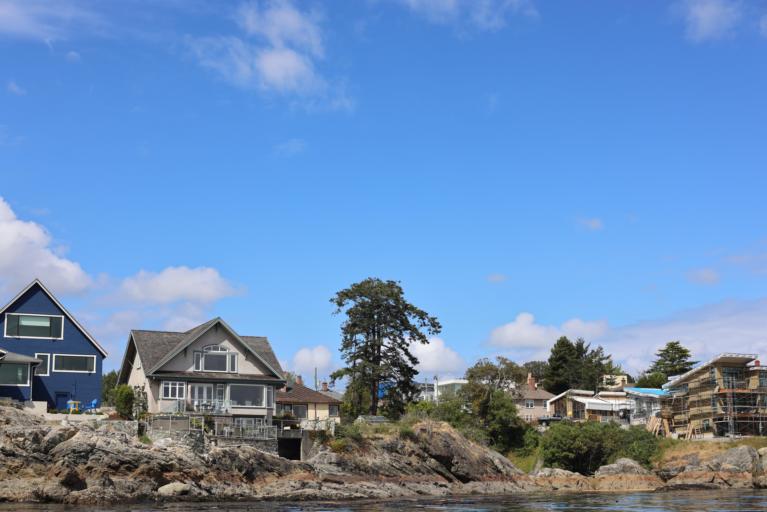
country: CA
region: British Columbia
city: Victoria
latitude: 48.4251
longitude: -123.4217
